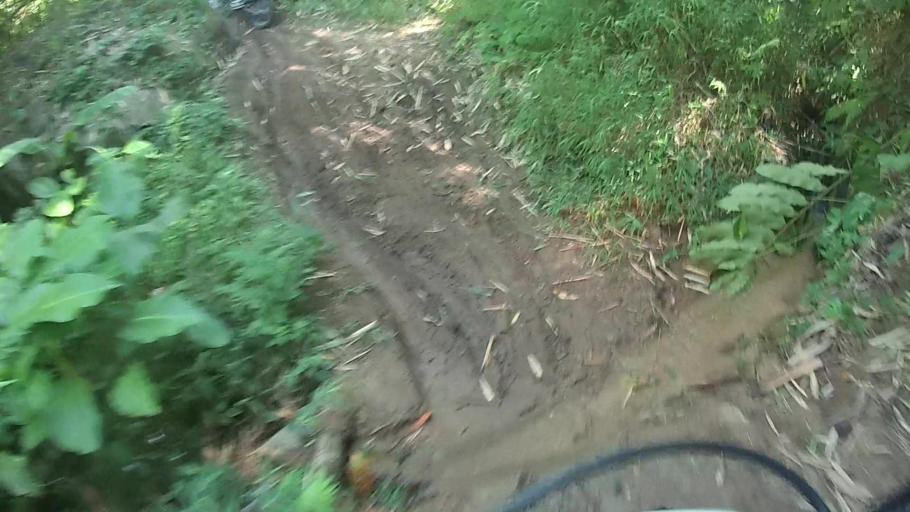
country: TH
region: Chiang Mai
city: Phrao
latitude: 19.5004
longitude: 99.2909
